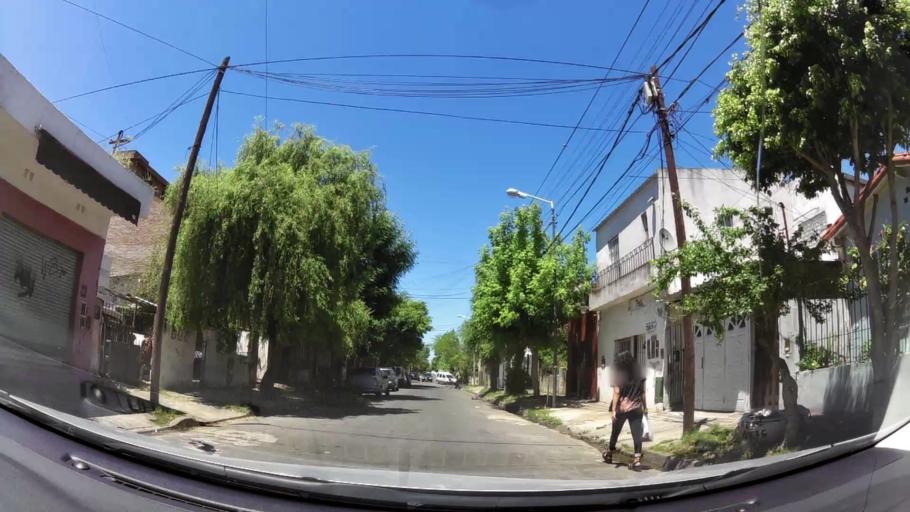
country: AR
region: Buenos Aires
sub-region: Partido de Tigre
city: Tigre
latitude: -34.4530
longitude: -58.5560
